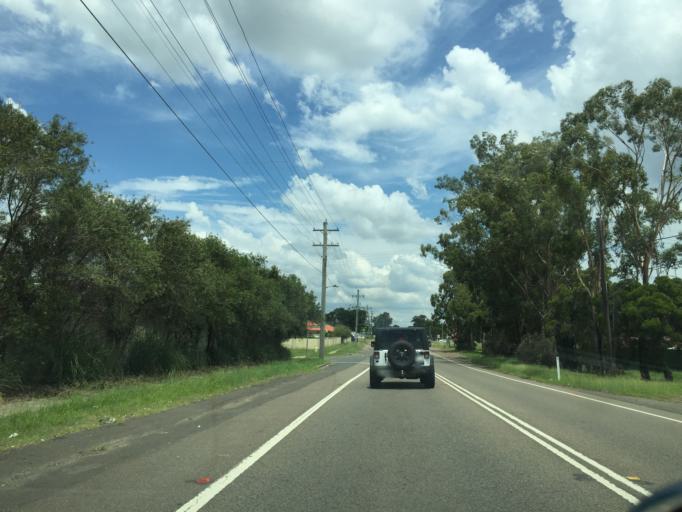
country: AU
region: New South Wales
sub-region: Blacktown
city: Hassall Grove
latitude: -33.7423
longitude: 150.8431
